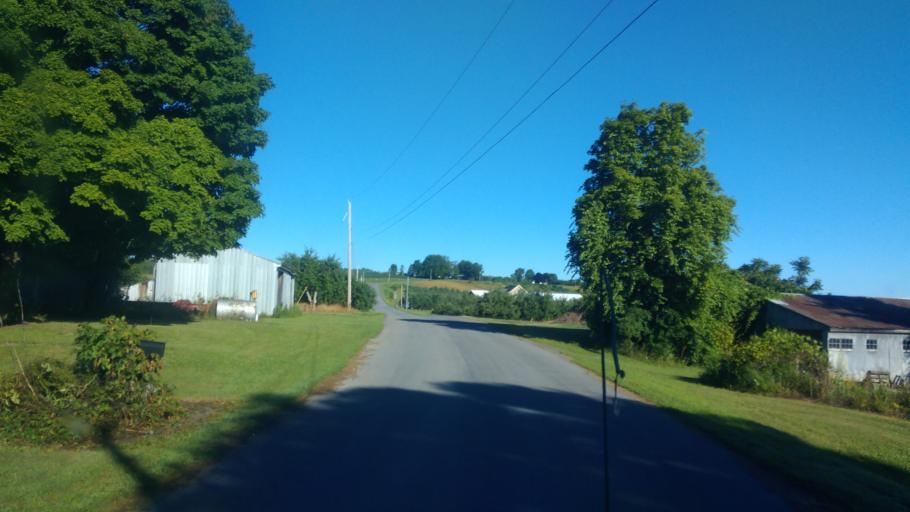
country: US
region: New York
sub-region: Wayne County
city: Sodus
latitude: 43.1994
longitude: -77.0955
